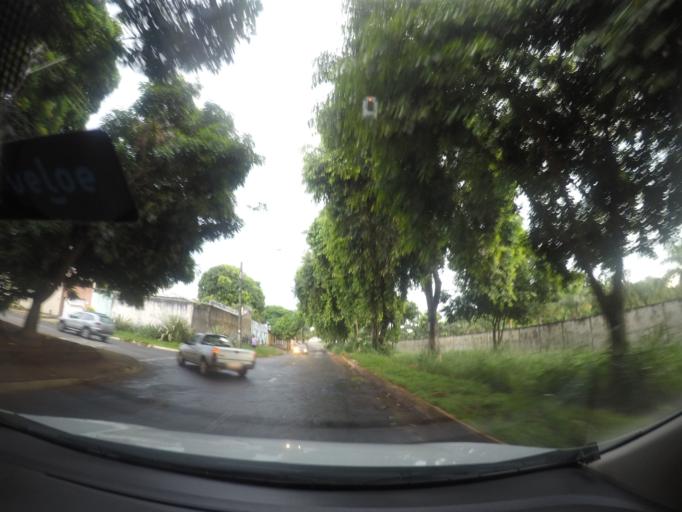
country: BR
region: Goias
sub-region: Goiania
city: Goiania
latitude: -16.7289
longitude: -49.3098
